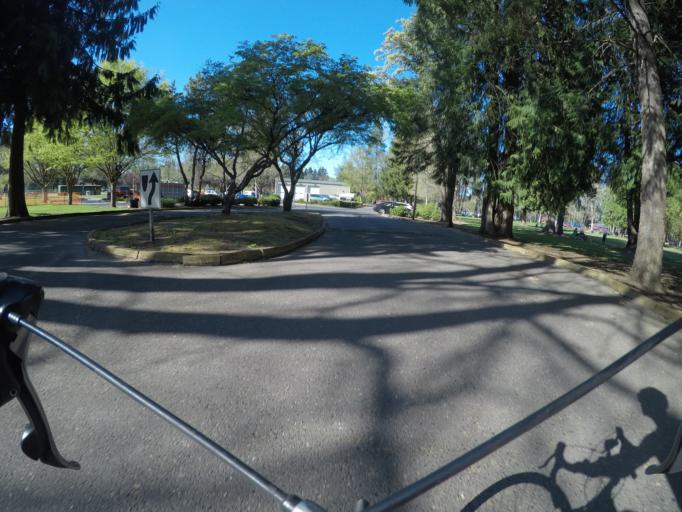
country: US
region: Oregon
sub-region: Washington County
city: Tualatin
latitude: 45.3958
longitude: -122.7727
